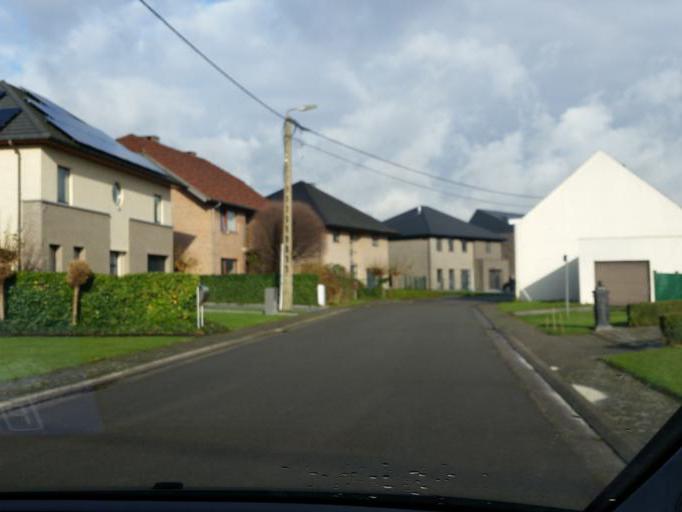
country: BE
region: Flanders
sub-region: Provincie Vlaams-Brabant
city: Zemst
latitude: 50.9643
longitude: 4.4443
